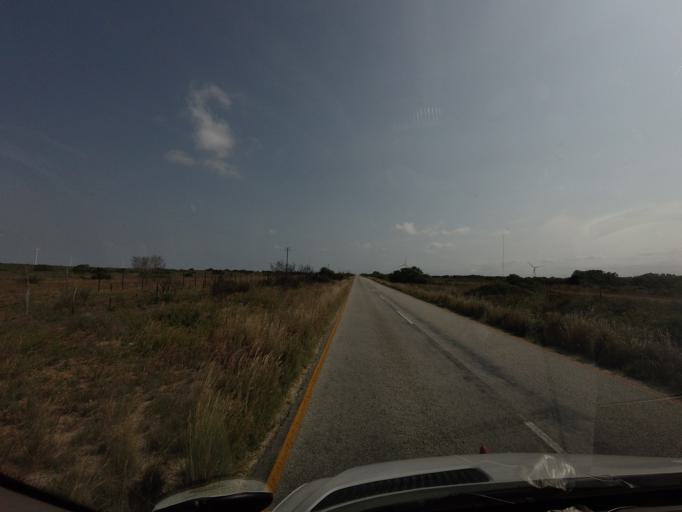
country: ZA
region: Eastern Cape
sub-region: Nelson Mandela Bay Metropolitan Municipality
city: Uitenhage
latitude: -33.6675
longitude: 25.5918
